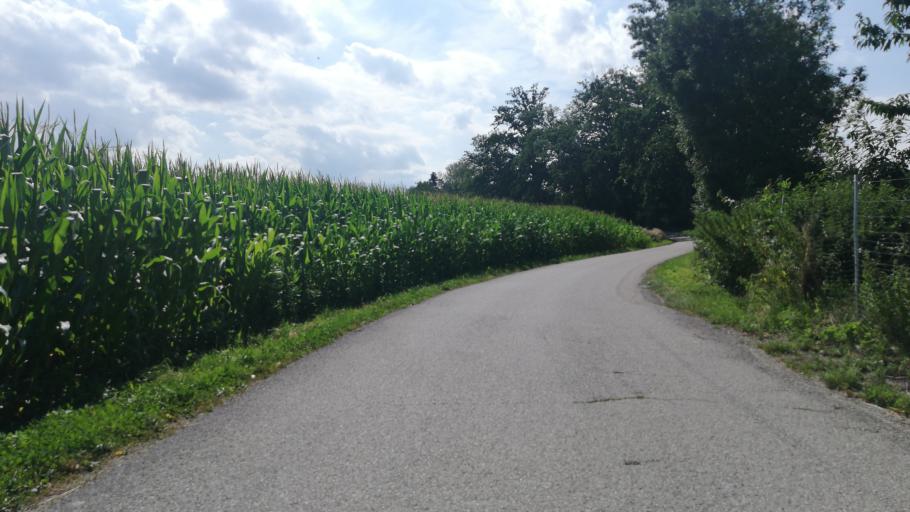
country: AT
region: Upper Austria
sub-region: Wels-Land
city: Pennewang
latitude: 48.1607
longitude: 13.8692
